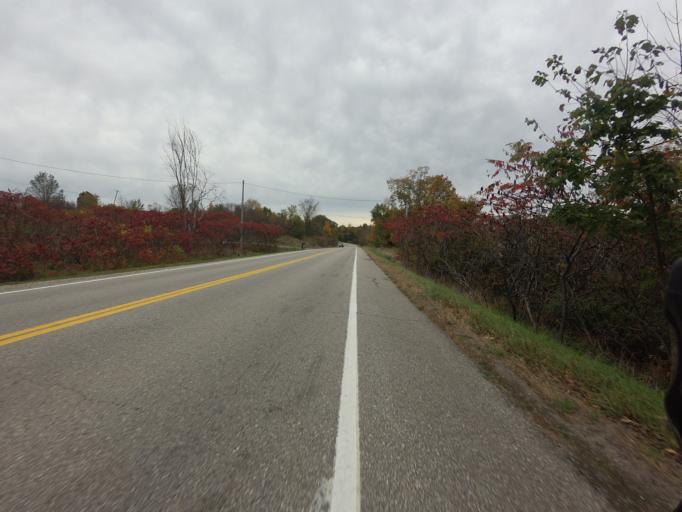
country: CA
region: Ontario
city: Gananoque
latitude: 44.5380
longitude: -76.1415
